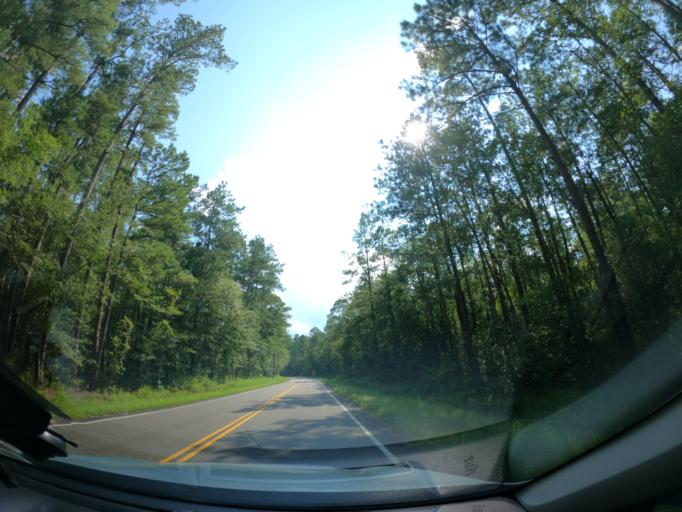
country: US
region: South Carolina
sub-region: Barnwell County
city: Williston
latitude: 33.5523
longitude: -81.4867
